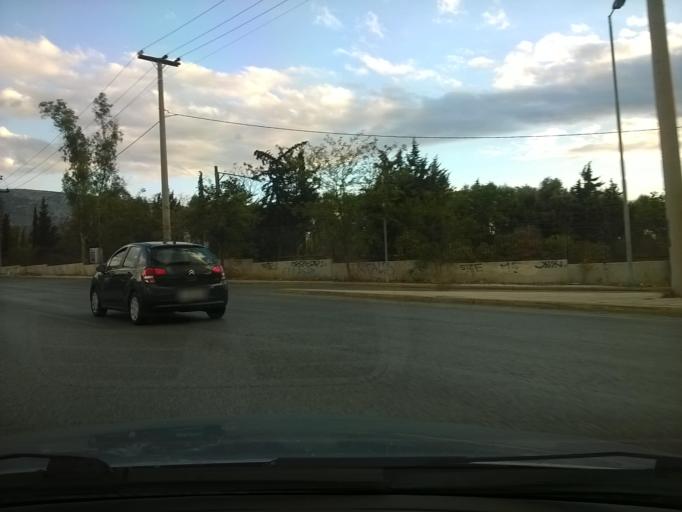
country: GR
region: Attica
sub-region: Nomarchia Athinas
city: Papagou
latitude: 37.9839
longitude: 23.7829
